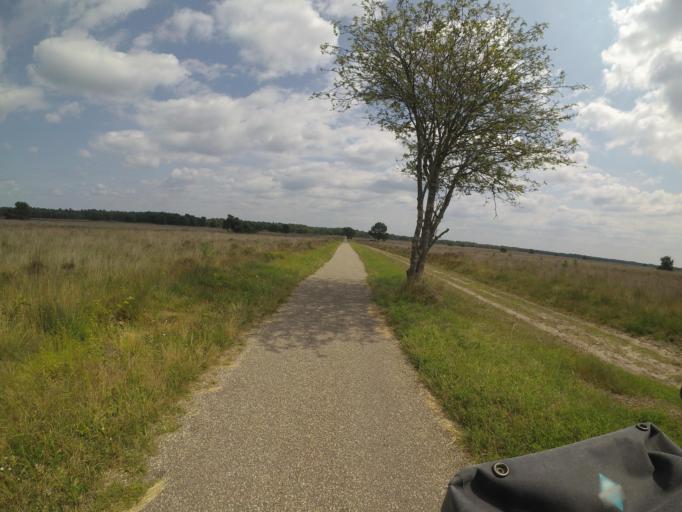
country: NL
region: Gelderland
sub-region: Gemeente Barneveld
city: Garderen
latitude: 52.2669
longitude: 5.7268
